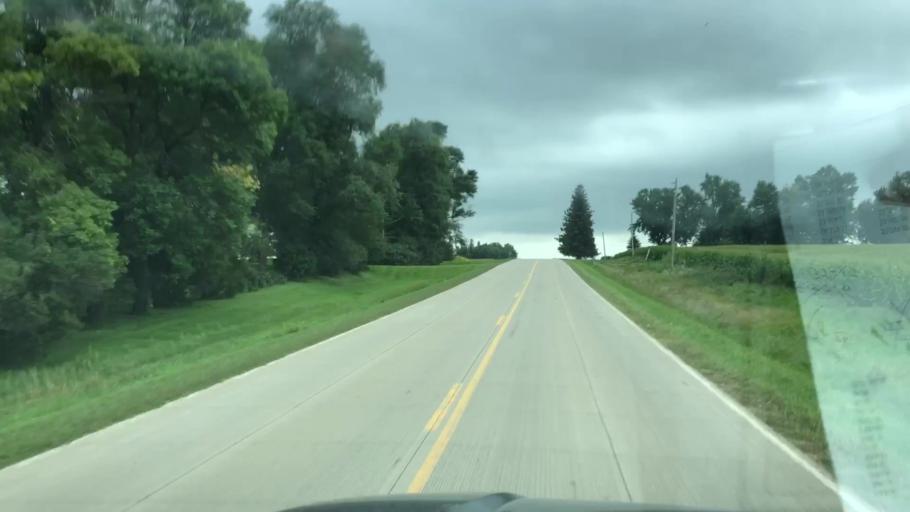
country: US
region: Iowa
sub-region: Sioux County
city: Alton
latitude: 43.1107
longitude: -95.9787
